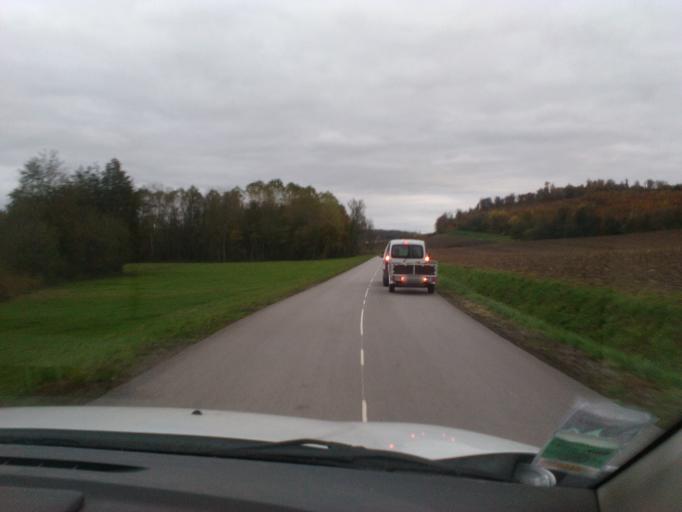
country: FR
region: Lorraine
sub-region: Departement des Vosges
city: Vincey
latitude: 48.2745
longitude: 6.2428
